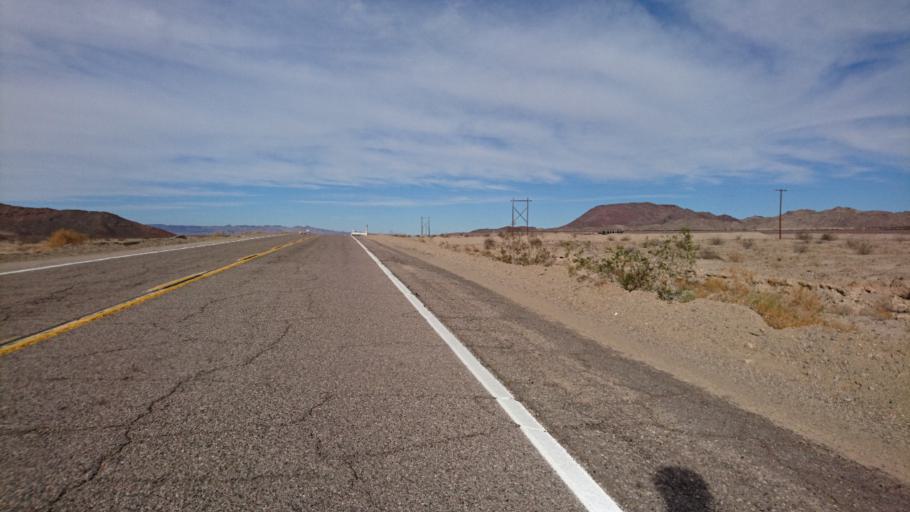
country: US
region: California
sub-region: San Bernardino County
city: Twentynine Palms
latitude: 34.5929
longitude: -115.9190
